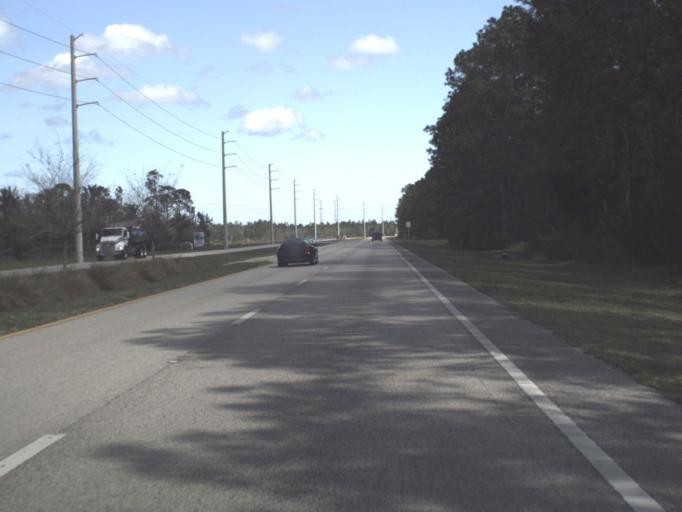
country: US
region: Florida
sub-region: Flagler County
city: Bunnell
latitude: 29.5086
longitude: -81.2641
